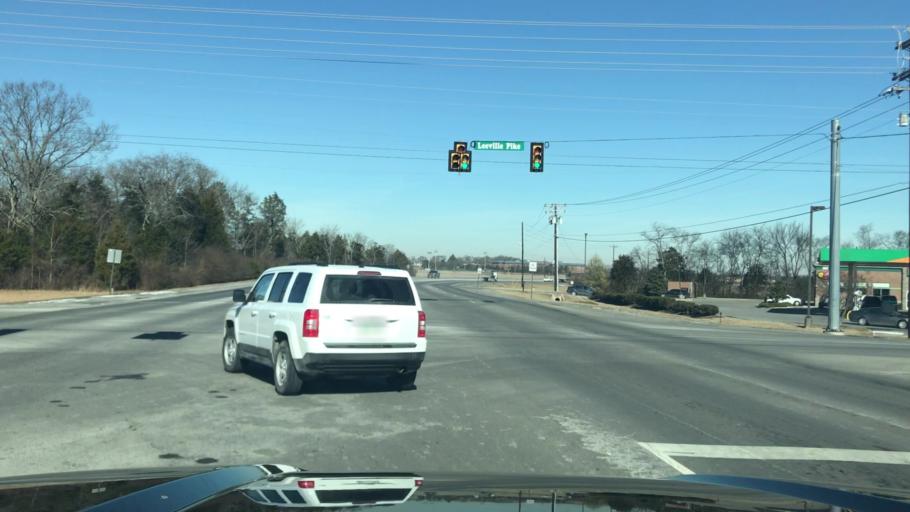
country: US
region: Tennessee
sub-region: Wilson County
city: Lebanon
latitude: 36.1953
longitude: -86.3329
